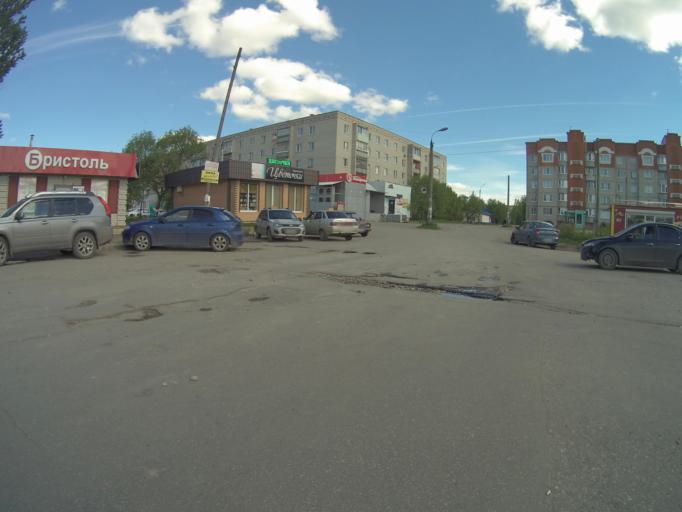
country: RU
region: Vladimir
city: Sudogda
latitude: 55.9517
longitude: 40.8762
